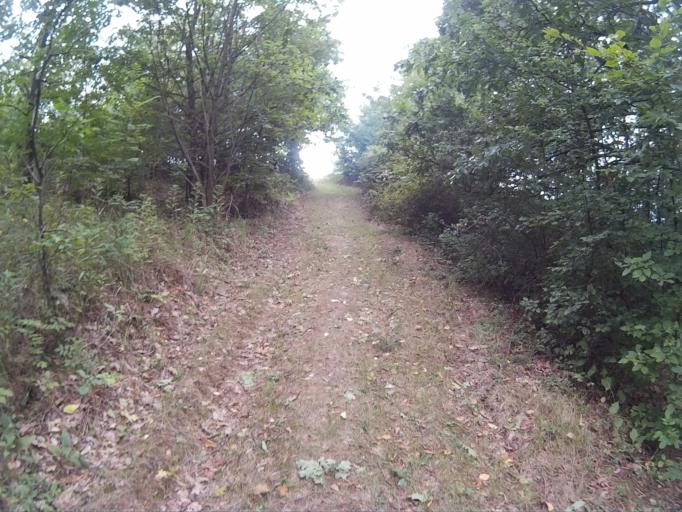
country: HU
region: Zala
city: Zalalovo
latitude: 46.8374
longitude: 16.5834
